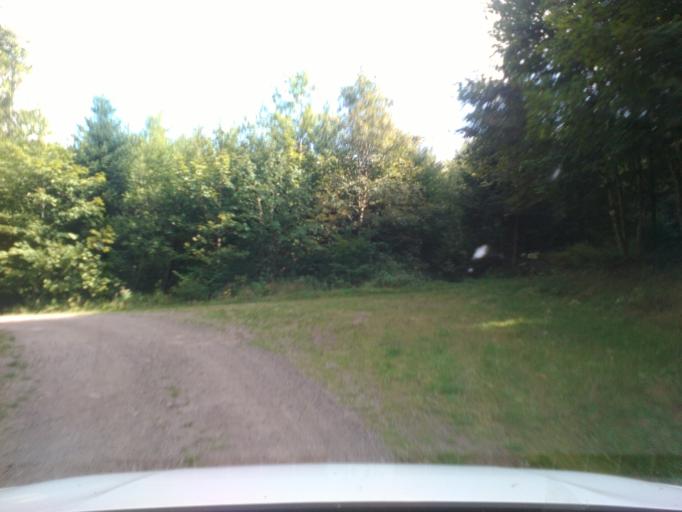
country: FR
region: Lorraine
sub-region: Departement des Vosges
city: Senones
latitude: 48.3518
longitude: 7.0490
